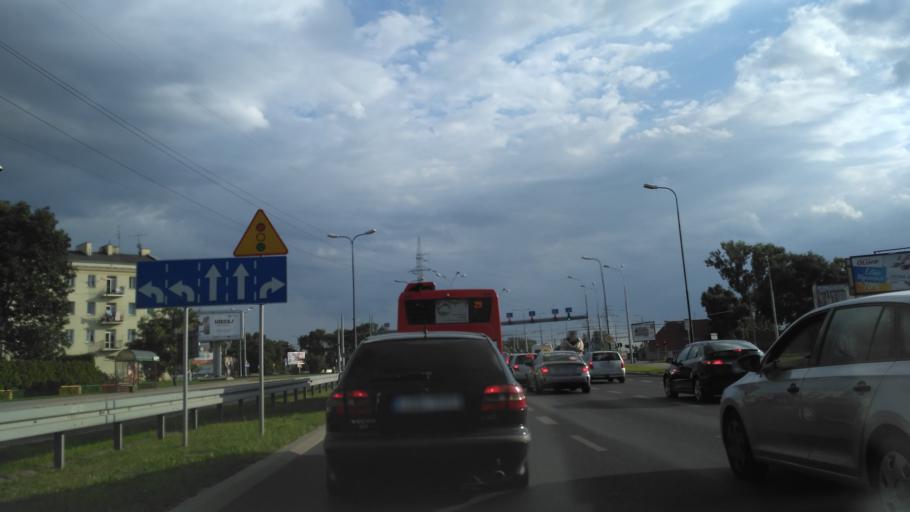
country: PL
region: Lublin Voivodeship
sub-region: Powiat lubelski
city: Lublin
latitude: 51.2360
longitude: 22.5693
